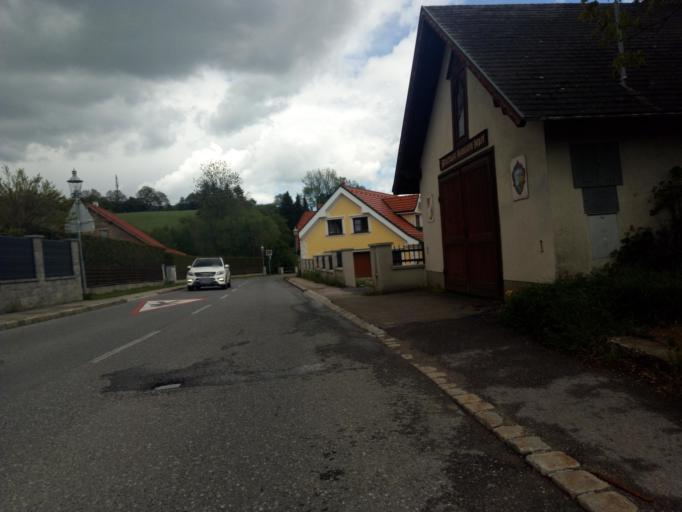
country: AT
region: Lower Austria
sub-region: Politischer Bezirk Modling
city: Breitenfurt bei Wien
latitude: 48.1391
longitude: 16.1460
